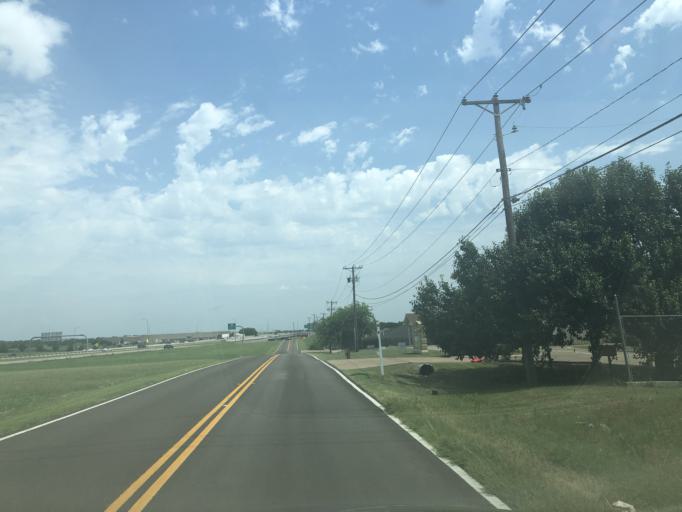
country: US
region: Texas
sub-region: Dallas County
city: Grand Prairie
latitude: 32.7236
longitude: -97.0196
